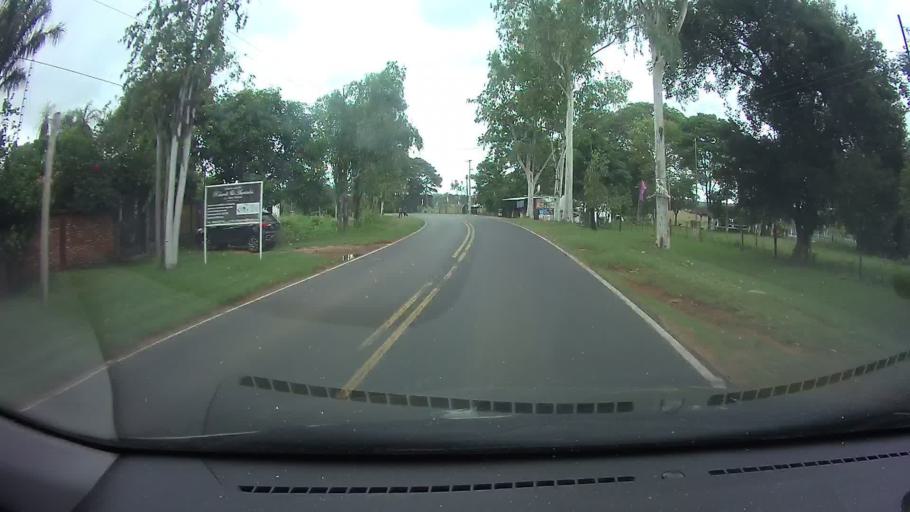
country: PY
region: Central
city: Nueva Italia
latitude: -25.5515
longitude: -57.5020
